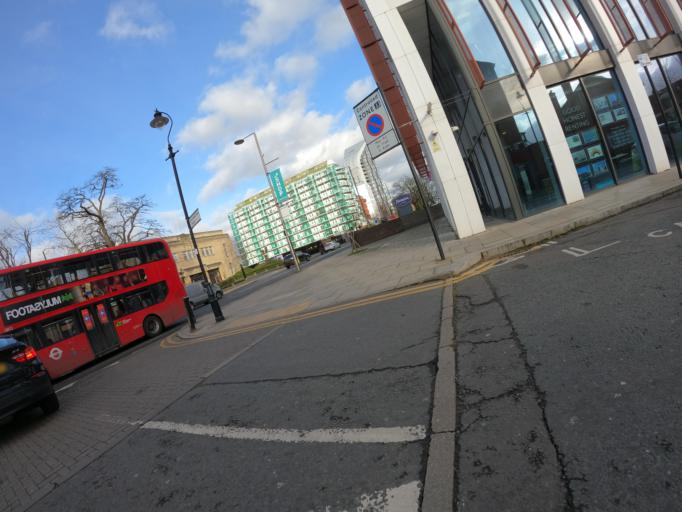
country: GB
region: England
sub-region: Greater London
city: Ealing
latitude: 51.5116
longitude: -0.3142
